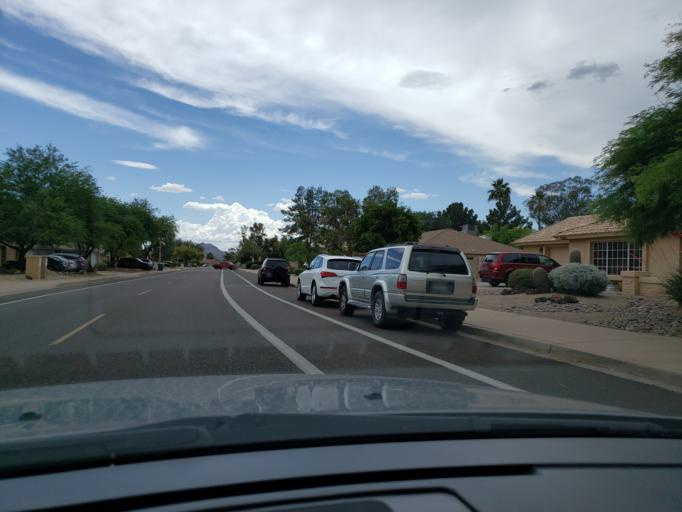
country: US
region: Arizona
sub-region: Maricopa County
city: Paradise Valley
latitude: 33.6238
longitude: -111.9519
